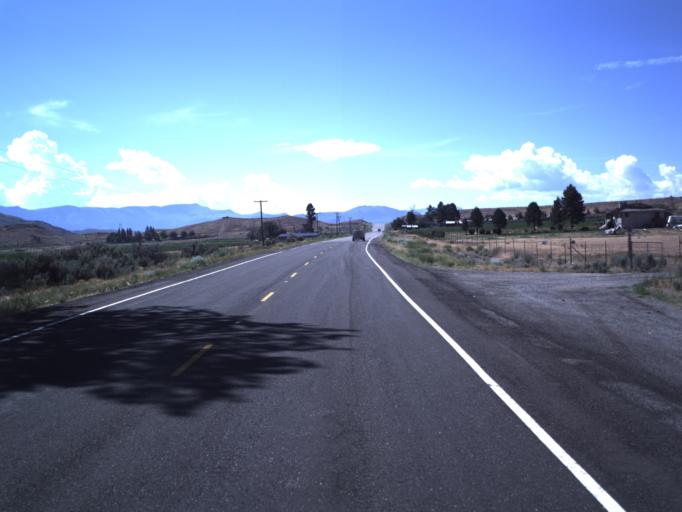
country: US
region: Utah
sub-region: Sevier County
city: Monroe
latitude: 38.4713
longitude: -112.2365
